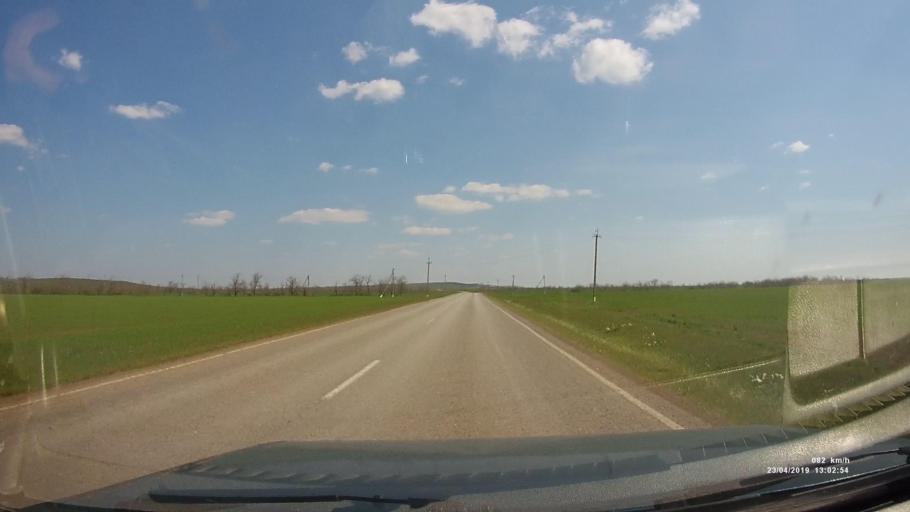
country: RU
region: Kalmykiya
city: Yashalta
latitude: 46.5987
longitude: 42.6758
